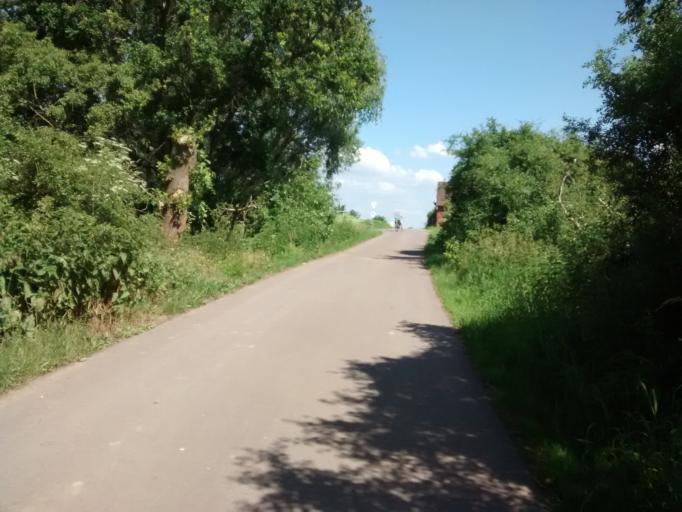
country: DE
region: Saxony-Anhalt
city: Wittenburg
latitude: 51.8455
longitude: 12.6162
